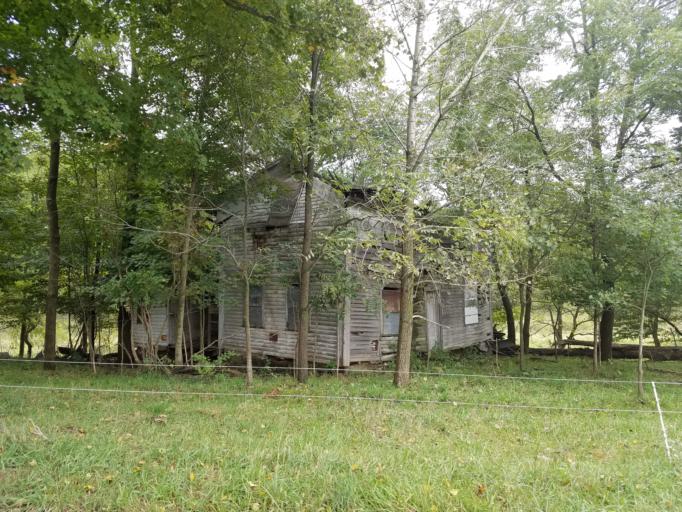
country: US
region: Ohio
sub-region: Knox County
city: Danville
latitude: 40.5459
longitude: -82.3299
